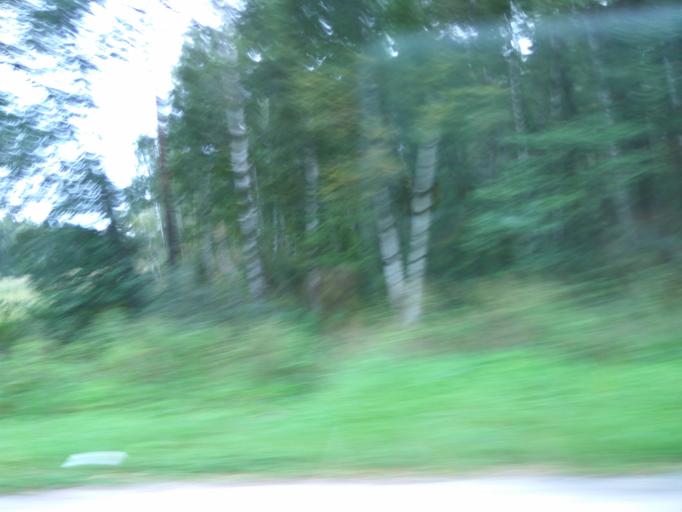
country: RU
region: Moskovskaya
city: Malyshevo
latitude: 55.5199
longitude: 38.3432
